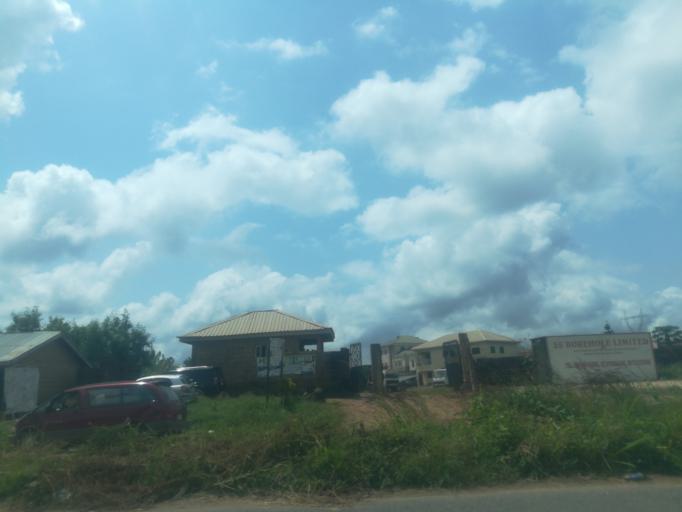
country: NG
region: Oyo
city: Ibadan
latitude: 7.3622
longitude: 3.8249
